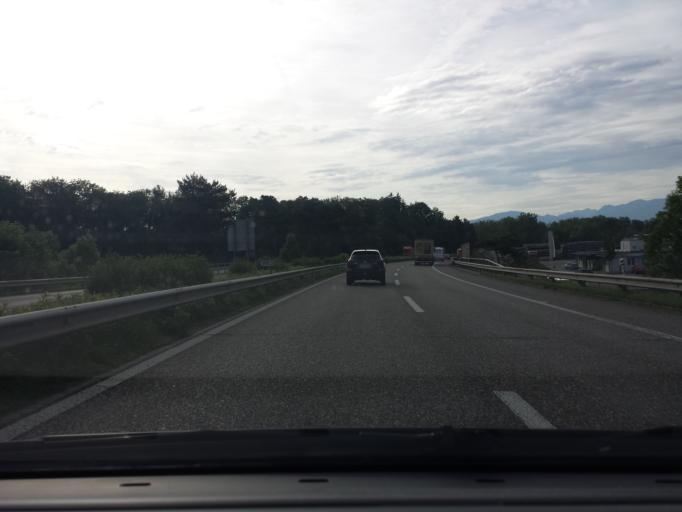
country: CH
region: Saint Gallen
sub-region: Wahlkreis Rheintal
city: Rheineck
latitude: 47.4804
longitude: 9.5789
